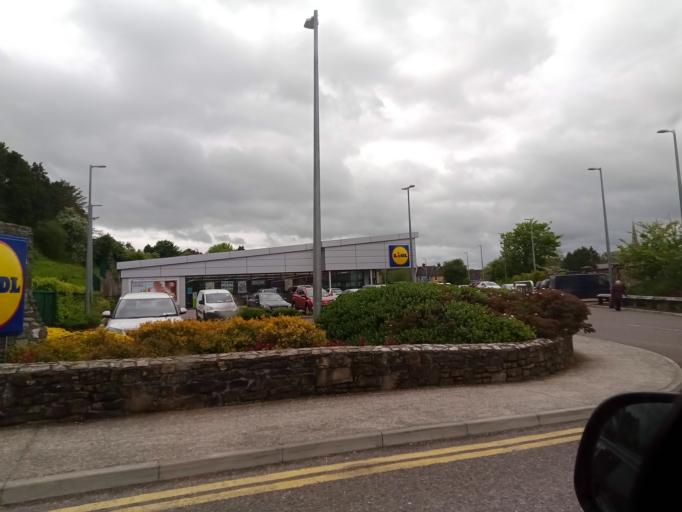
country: IE
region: Munster
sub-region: County Cork
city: Clonakilty
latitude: 51.6206
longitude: -8.8863
